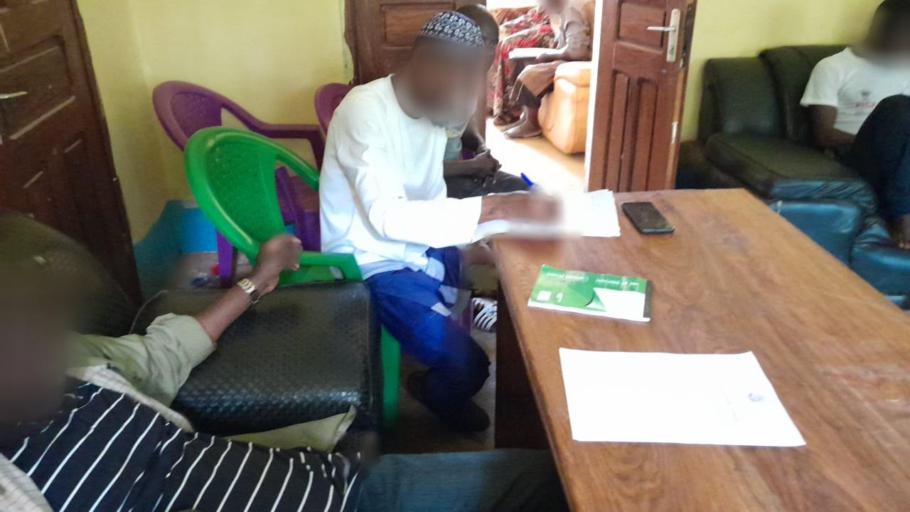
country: GN
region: Boke
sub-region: Boke Prefecture
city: Boke
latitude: 11.1922
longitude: -14.5399
